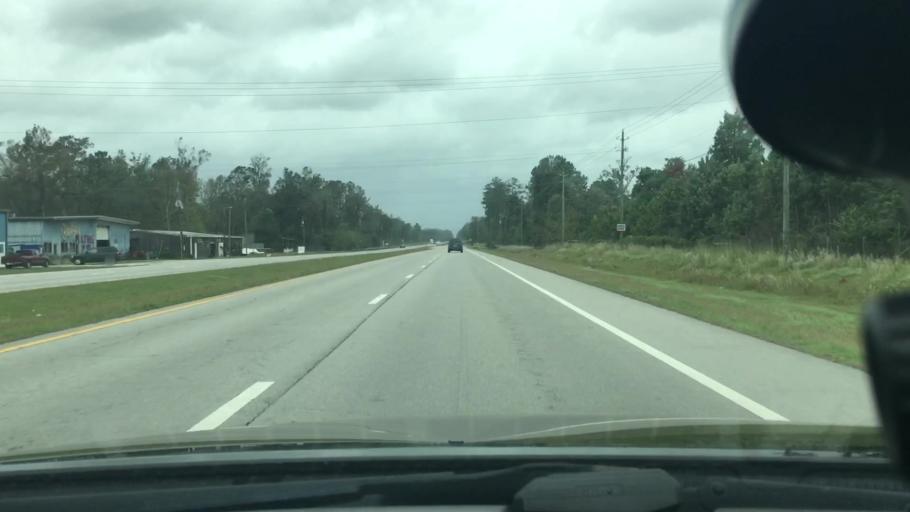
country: US
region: North Carolina
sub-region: Craven County
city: New Bern
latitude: 35.1429
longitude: -77.0303
